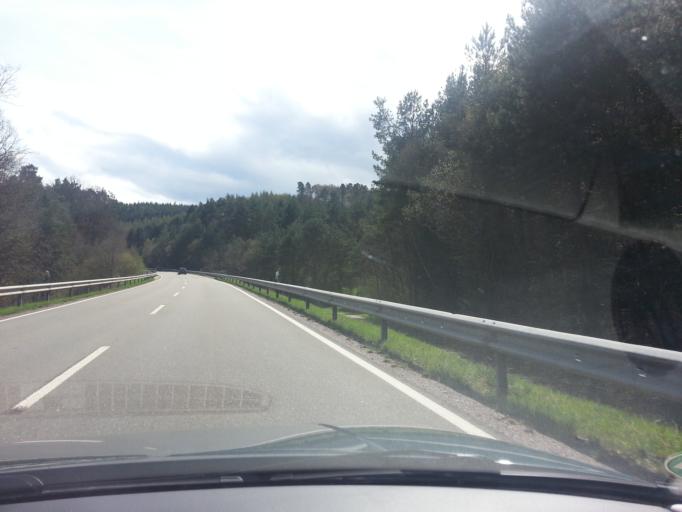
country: DE
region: Rheinland-Pfalz
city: Munchweiler an der Rodalbe
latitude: 49.2255
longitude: 7.6921
